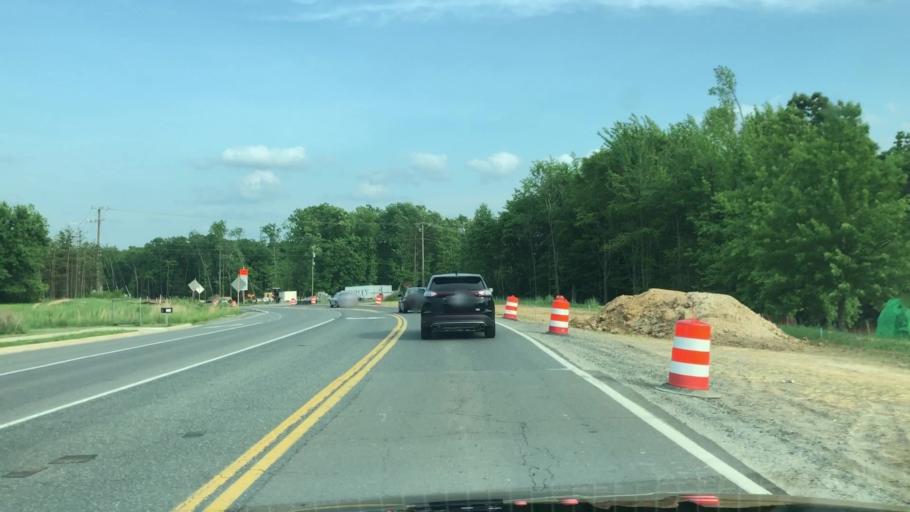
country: US
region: Virginia
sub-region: Stafford County
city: Stafford
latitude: 38.4349
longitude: -77.4493
